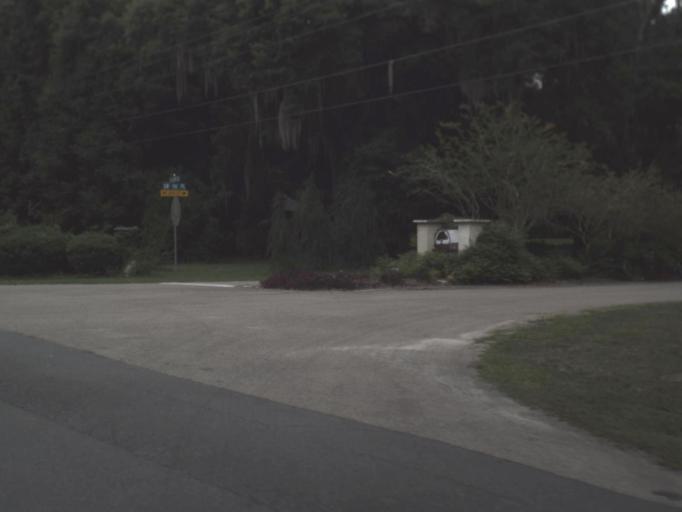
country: US
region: Florida
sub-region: Alachua County
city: Gainesville
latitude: 29.5643
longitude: -82.3926
